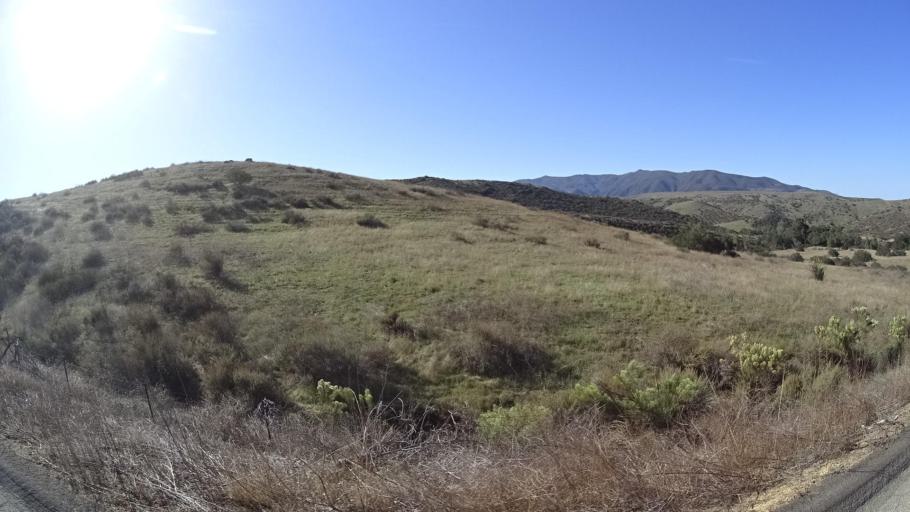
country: US
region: California
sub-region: San Diego County
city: Jamul
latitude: 32.6730
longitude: -116.8088
